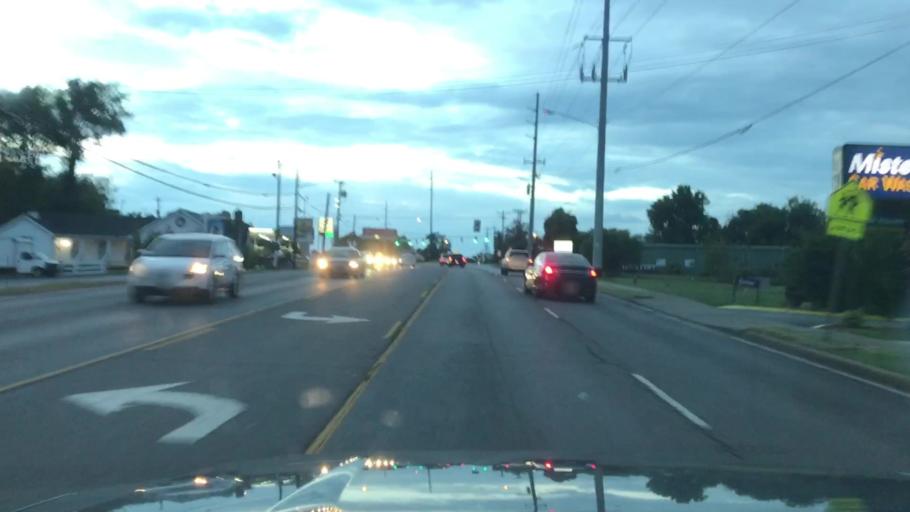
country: US
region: Tennessee
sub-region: Rutherford County
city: La Vergne
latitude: 36.0929
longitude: -86.6523
